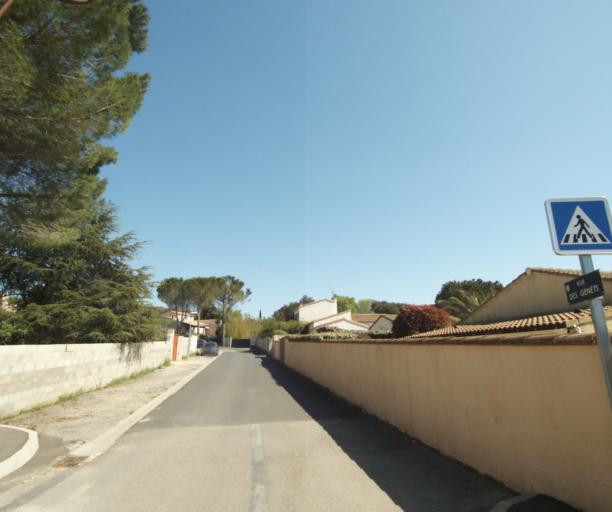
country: FR
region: Languedoc-Roussillon
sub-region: Departement de l'Herault
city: Sussargues
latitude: 43.7135
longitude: 3.9955
